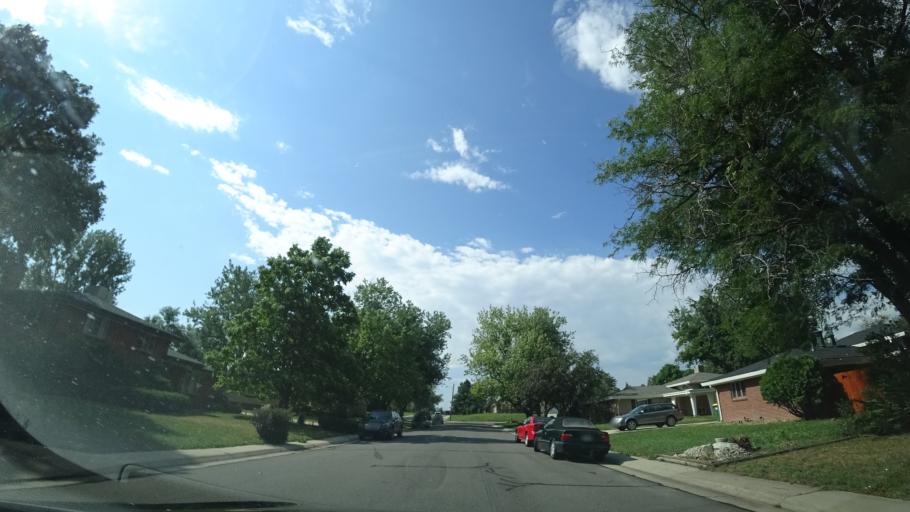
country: US
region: Colorado
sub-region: Jefferson County
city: Lakewood
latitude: 39.7140
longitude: -105.0571
